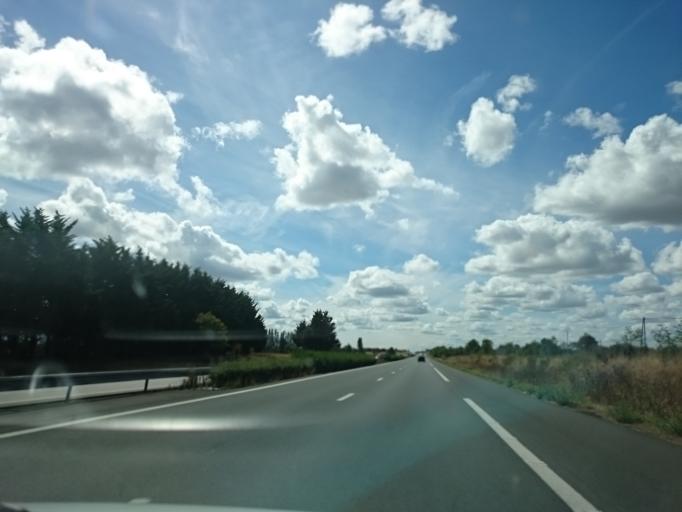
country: FR
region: Pays de la Loire
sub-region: Departement de la Loire-Atlantique
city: Saint-Herblon
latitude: 47.4167
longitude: -1.1283
